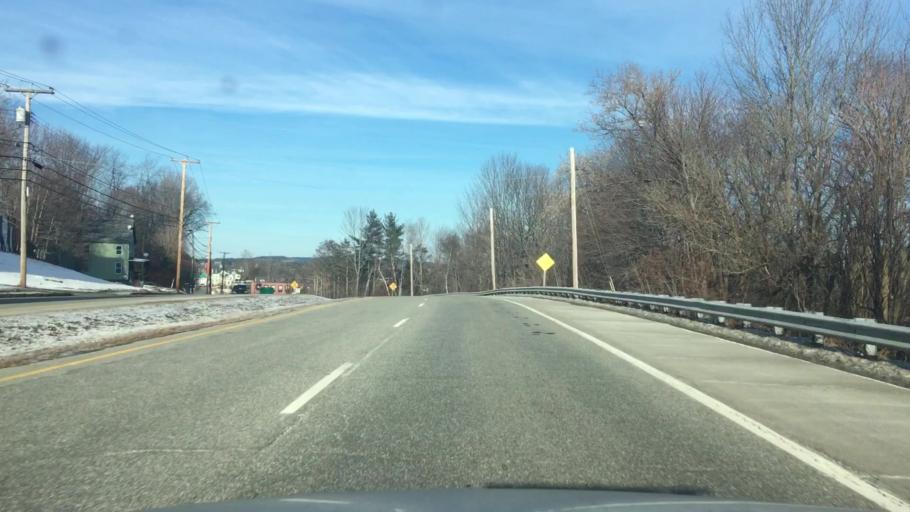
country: US
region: Maine
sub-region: Androscoggin County
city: Auburn
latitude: 44.0839
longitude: -70.2326
